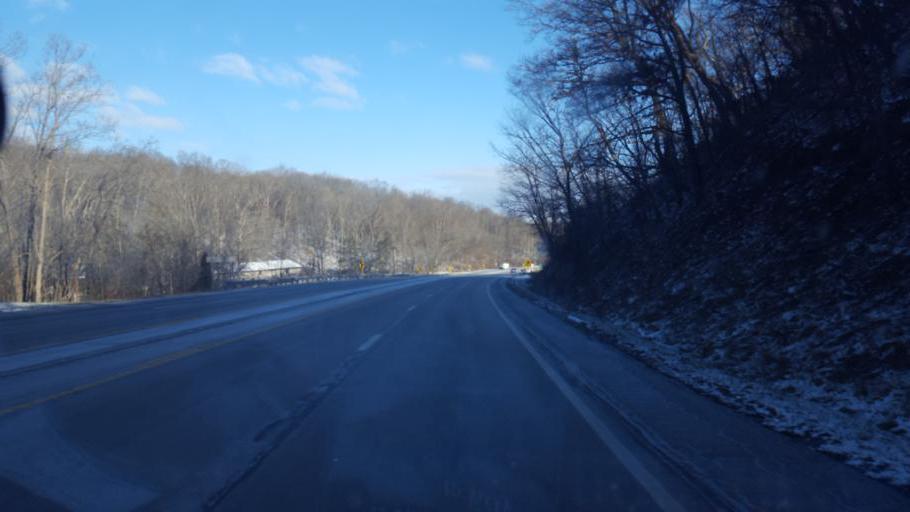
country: US
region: Ohio
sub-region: Pike County
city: Waverly
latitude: 39.2185
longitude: -82.9841
